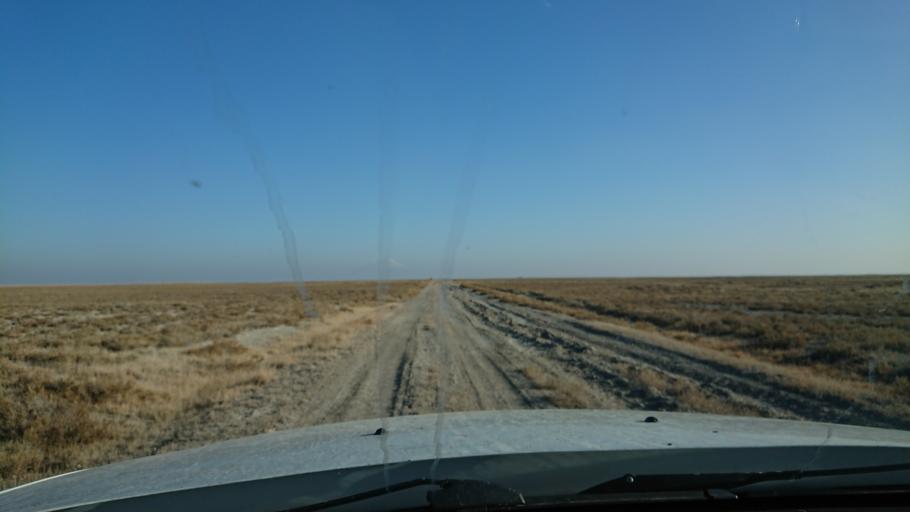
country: TR
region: Aksaray
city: Eskil
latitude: 38.4057
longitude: 33.5721
